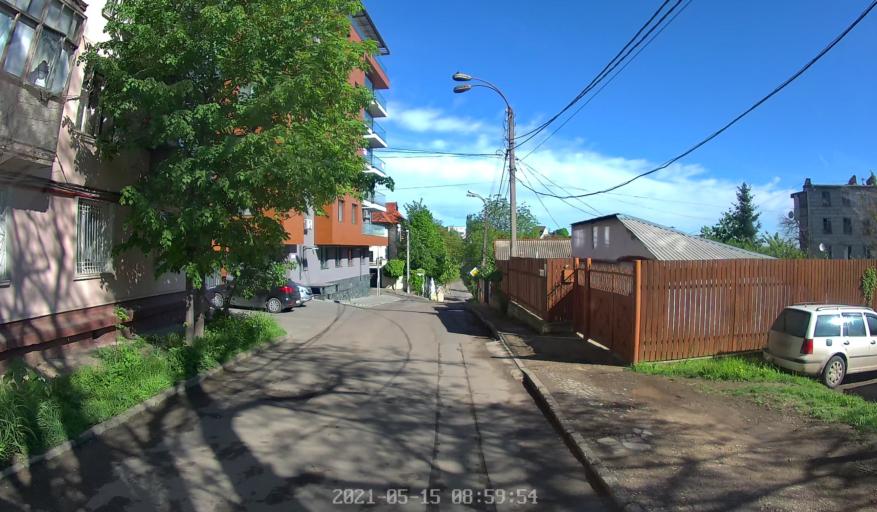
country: MD
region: Chisinau
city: Chisinau
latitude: 47.0061
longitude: 28.8228
